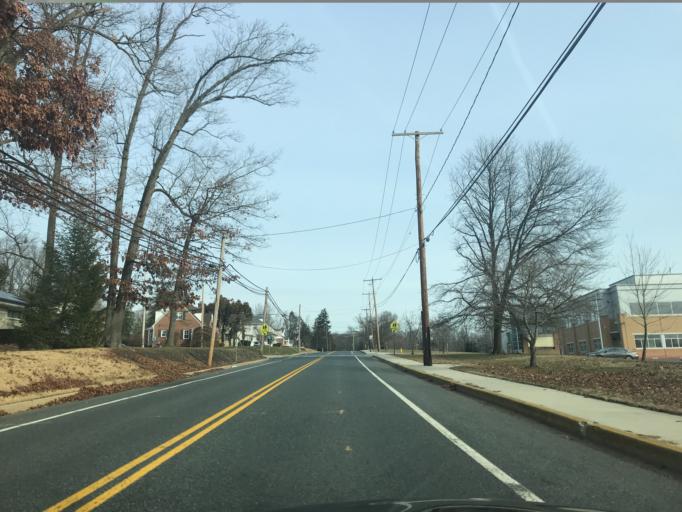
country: US
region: Maryland
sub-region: Harford County
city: Aberdeen
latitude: 39.5154
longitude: -76.1734
